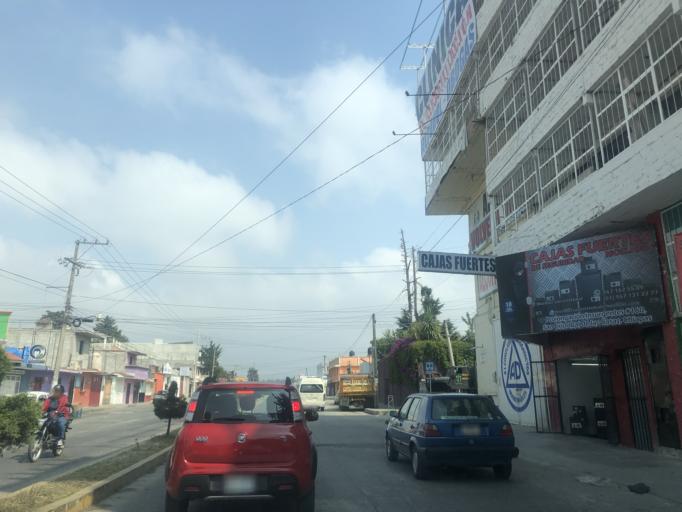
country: MX
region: Chiapas
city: San Cristobal de las Casas
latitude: 16.7135
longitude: -92.6338
